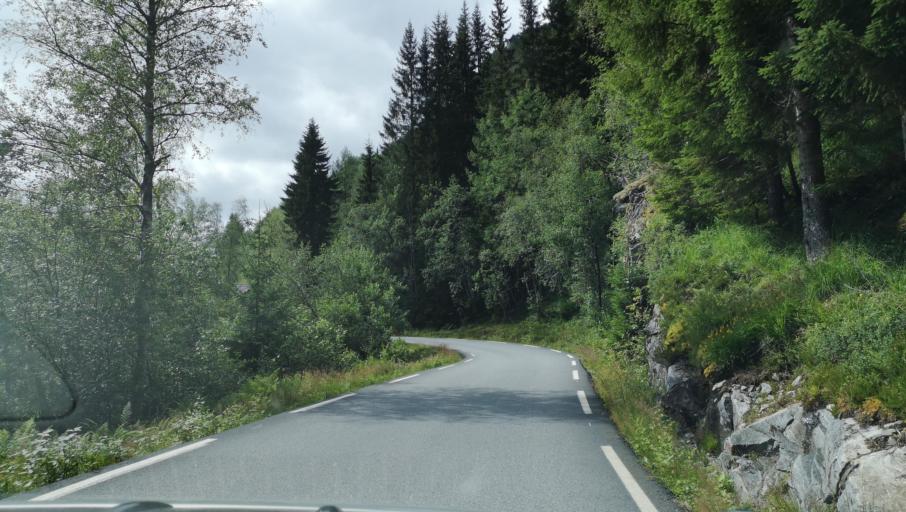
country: NO
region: Hordaland
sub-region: Modalen
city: Mo
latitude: 60.7862
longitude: 5.9342
